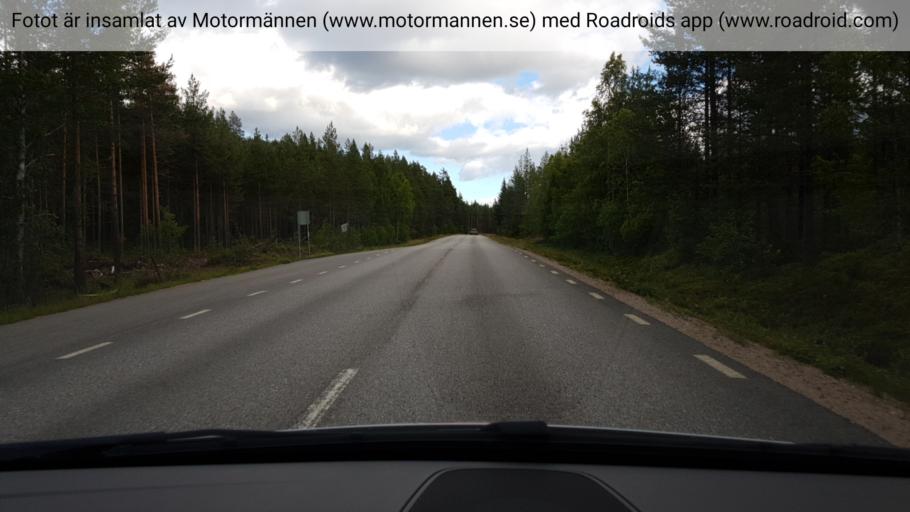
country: SE
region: Jaemtland
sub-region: Harjedalens Kommun
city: Sveg
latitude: 62.0271
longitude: 14.8049
